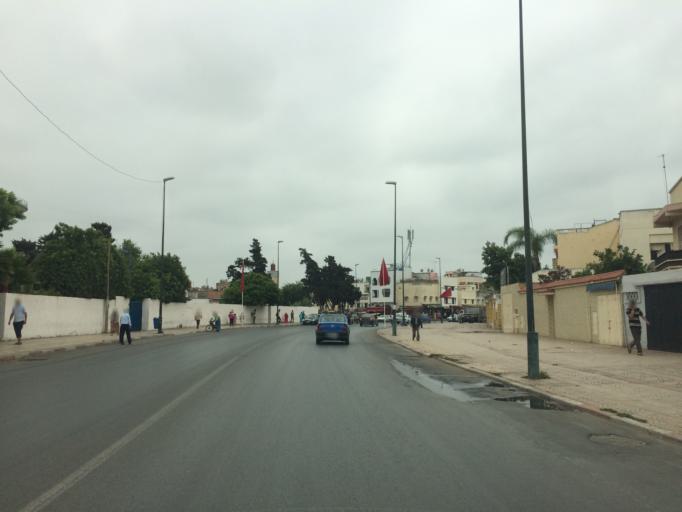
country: MA
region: Rabat-Sale-Zemmour-Zaer
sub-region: Rabat
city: Rabat
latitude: 33.9884
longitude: -6.8181
